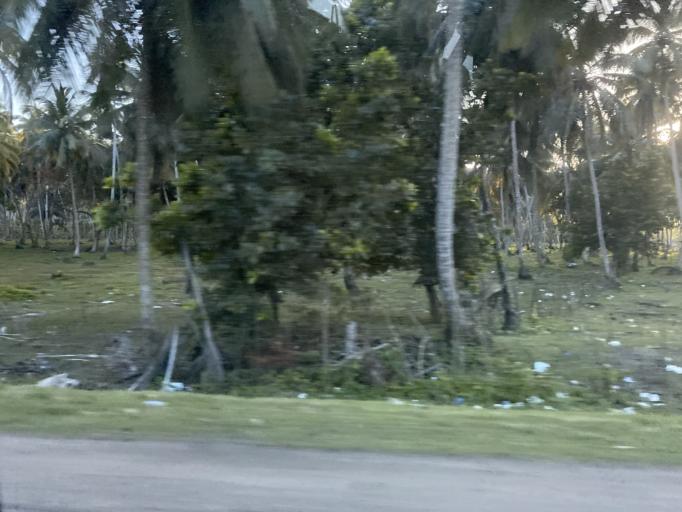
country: DO
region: Maria Trinidad Sanchez
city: Nagua
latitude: 19.3644
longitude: -69.8357
